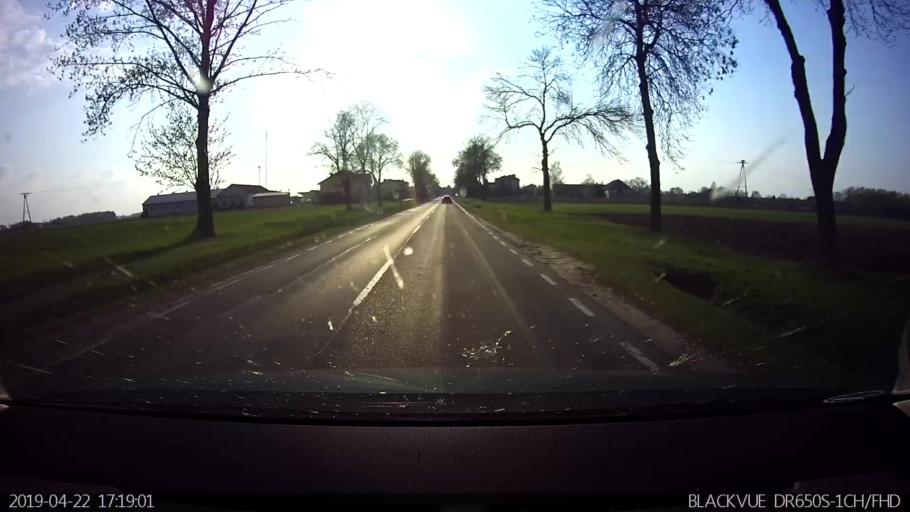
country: PL
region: Masovian Voivodeship
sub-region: Powiat sokolowski
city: Repki
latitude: 52.3850
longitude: 22.4013
